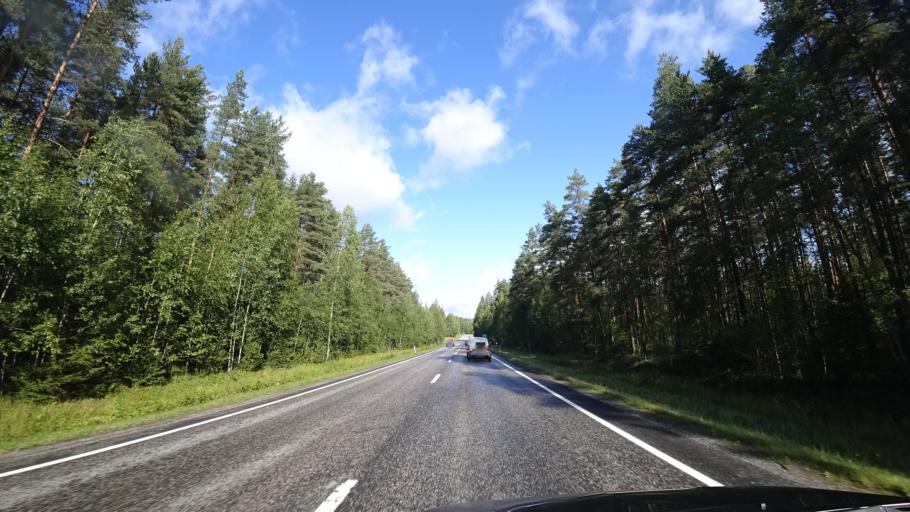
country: FI
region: Uusimaa
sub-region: Helsinki
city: Tuusula
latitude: 60.4553
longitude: 24.9532
